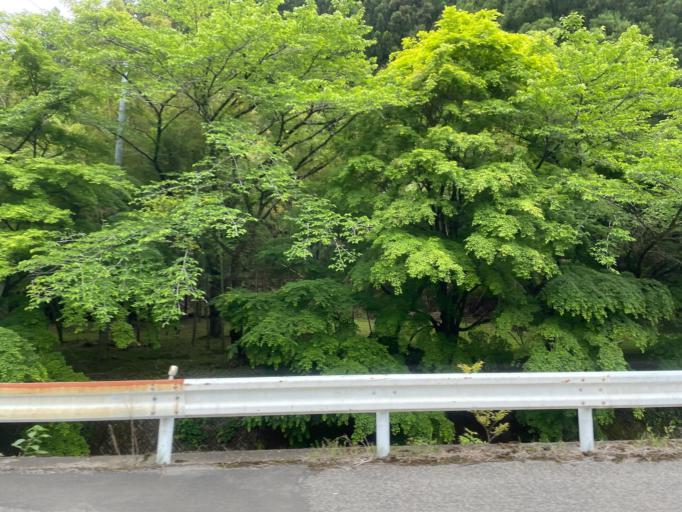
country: JP
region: Tochigi
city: Tanuma
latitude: 36.4693
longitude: 139.5971
